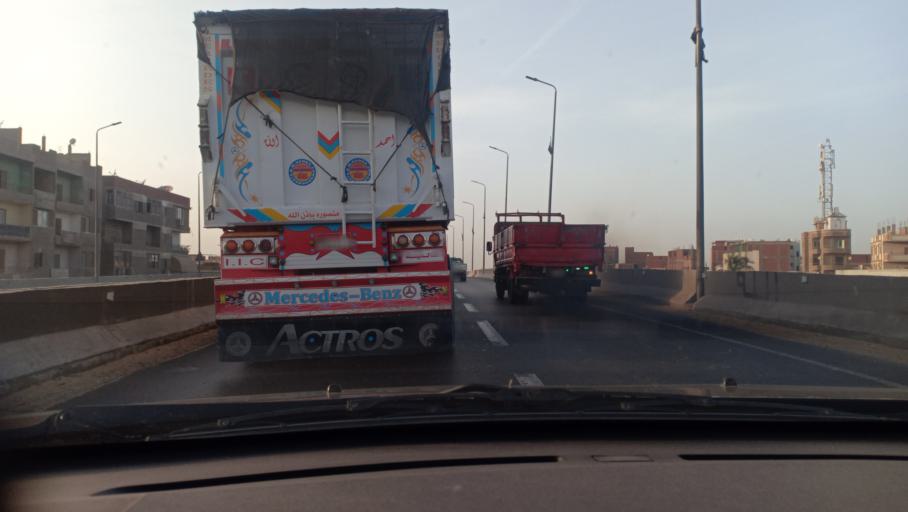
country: EG
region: Muhafazat al Minufiyah
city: Quwaysina
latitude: 30.5478
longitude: 31.2691
